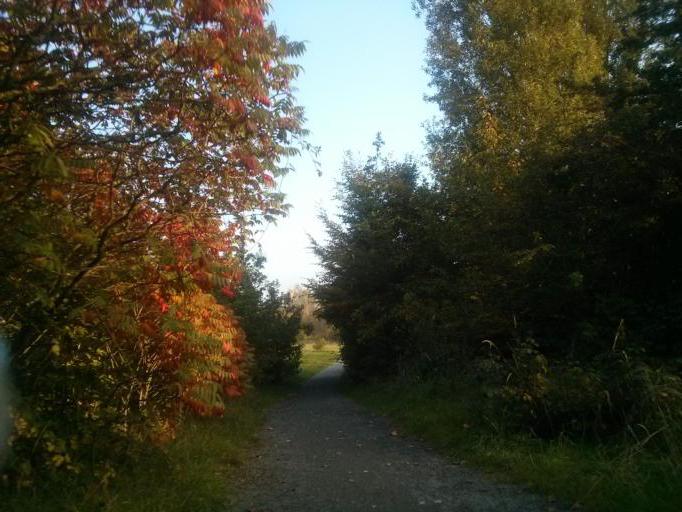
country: DE
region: North Rhine-Westphalia
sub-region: Regierungsbezirk Koln
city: Poll
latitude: 50.9049
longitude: 7.0088
